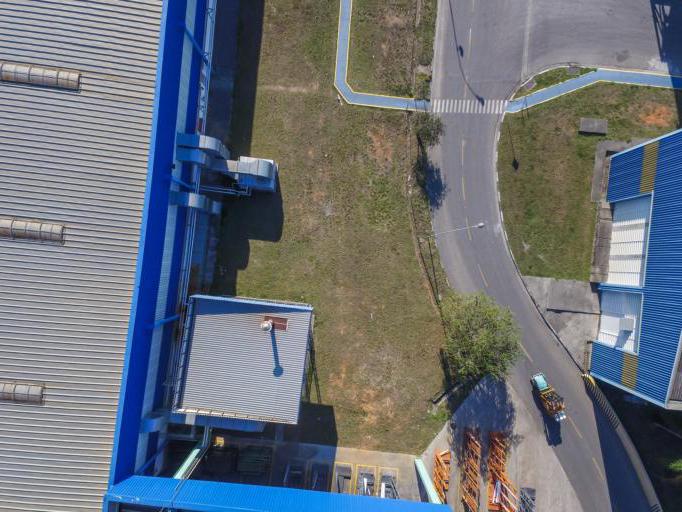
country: BR
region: Sao Paulo
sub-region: Jacarei
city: Jacarei
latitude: -23.2929
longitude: -45.9334
